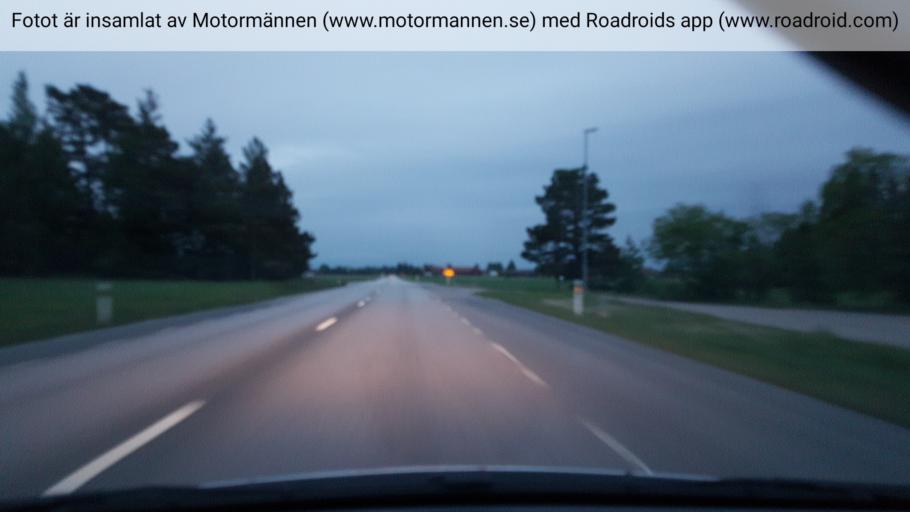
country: SE
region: Vaestmanland
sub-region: Sala Kommun
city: Sala
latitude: 59.8735
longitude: 16.6267
